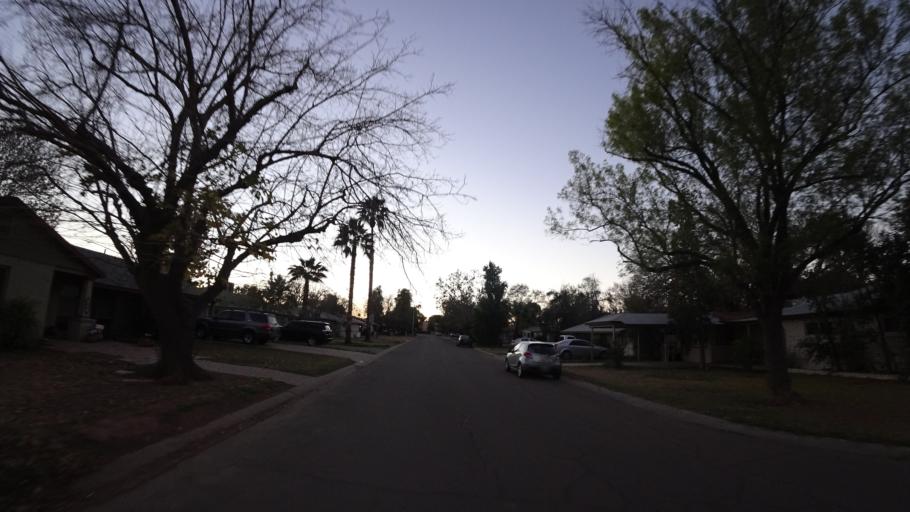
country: US
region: Arizona
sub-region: Maricopa County
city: Tempe Junction
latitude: 33.4139
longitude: -111.9459
